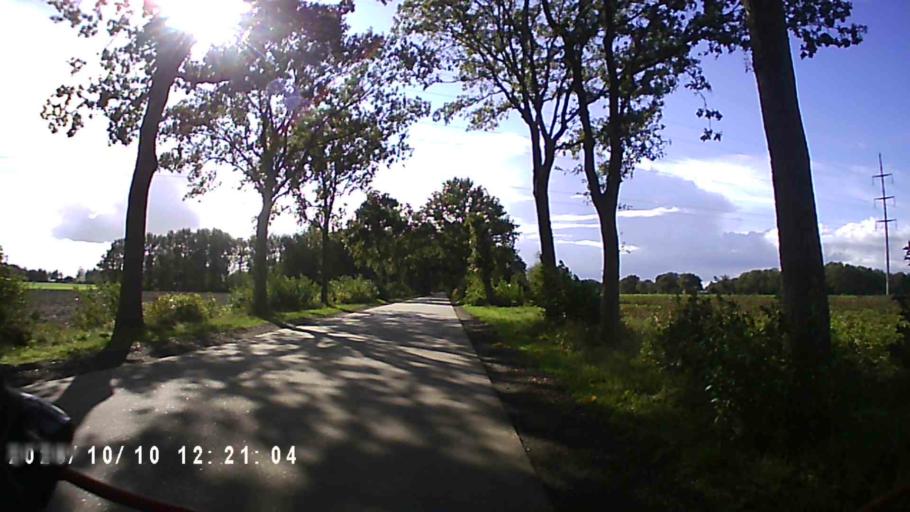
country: NL
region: Friesland
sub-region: Gemeente Heerenveen
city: Jubbega
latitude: 53.0063
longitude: 6.1806
